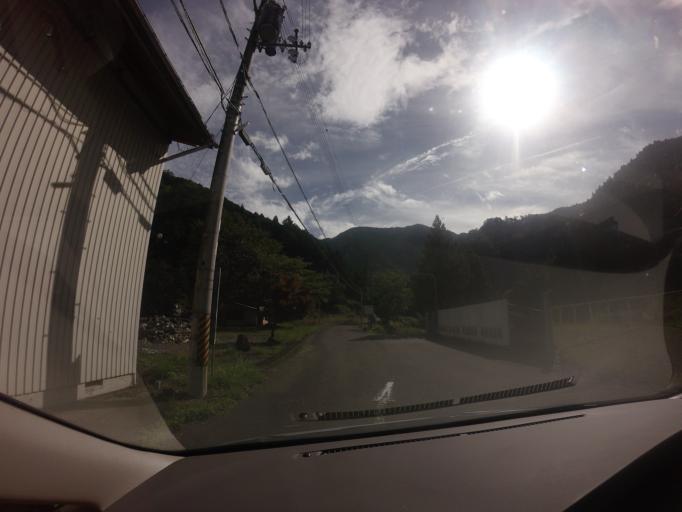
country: JP
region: Wakayama
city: Shingu
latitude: 33.9706
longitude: 135.8477
